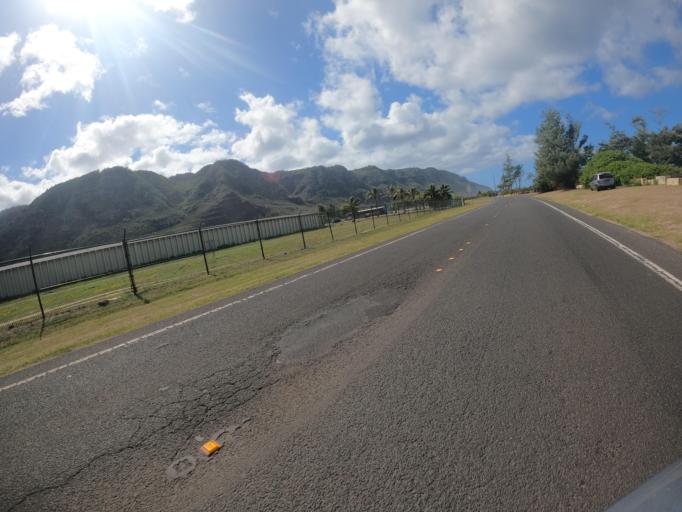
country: US
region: Hawaii
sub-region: Honolulu County
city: Mokuleia
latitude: 21.5834
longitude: -158.2079
